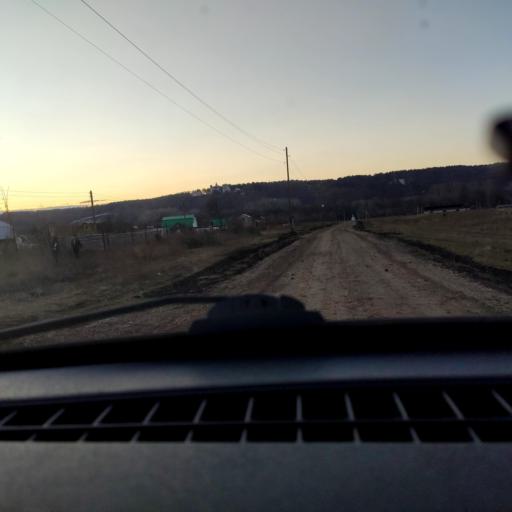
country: RU
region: Bashkortostan
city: Ufa
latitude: 54.7362
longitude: 56.0509
